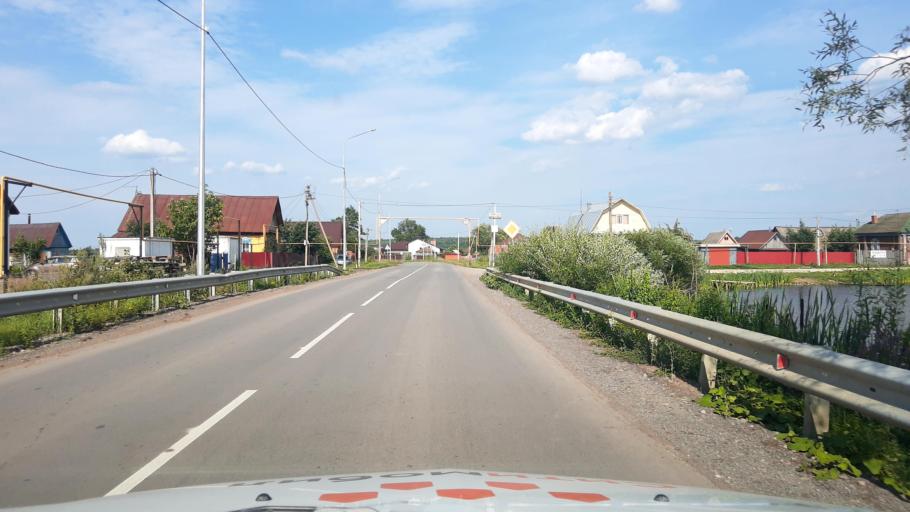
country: RU
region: Bashkortostan
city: Kabakovo
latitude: 54.6571
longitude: 56.1957
